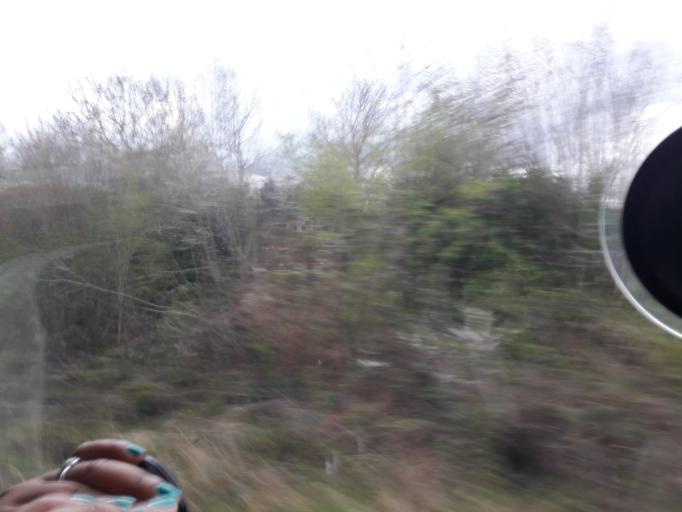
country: IE
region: Leinster
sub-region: An Longfort
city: Longford
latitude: 53.7403
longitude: -7.8219
